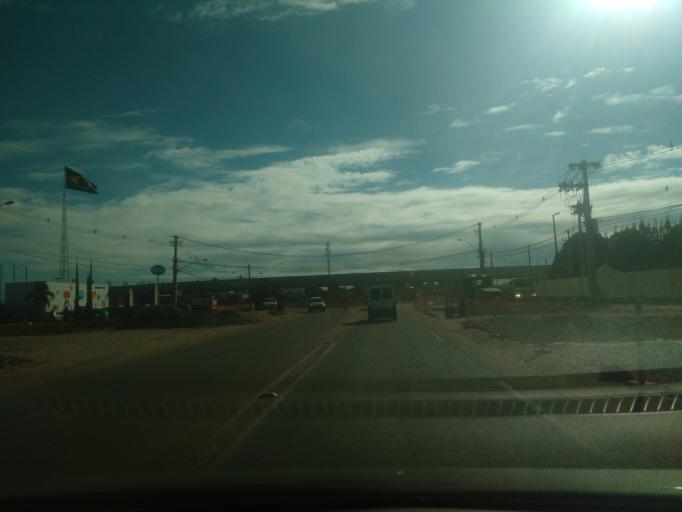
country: BR
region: Alagoas
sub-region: Satuba
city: Satuba
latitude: -9.5652
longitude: -35.7756
